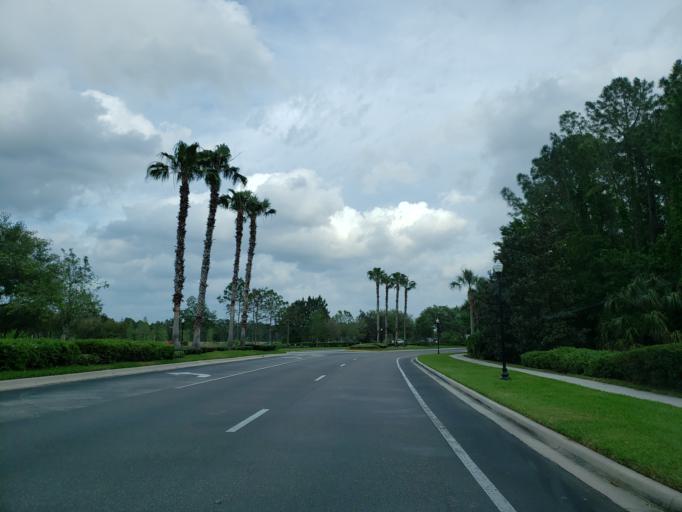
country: US
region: Florida
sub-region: Pasco County
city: Wesley Chapel
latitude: 28.2099
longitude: -82.3559
